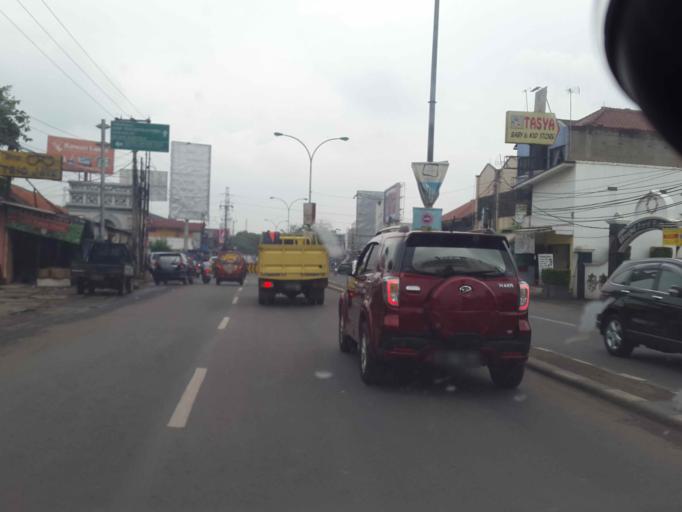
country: ID
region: West Java
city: Cikarang
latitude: -6.2961
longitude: 107.1473
